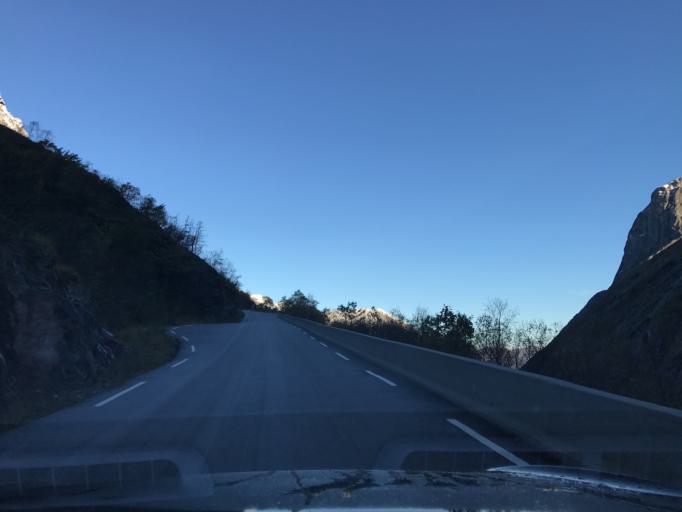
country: NO
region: More og Romsdal
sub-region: Rauma
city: Andalsnes
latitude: 62.4575
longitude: 7.6722
